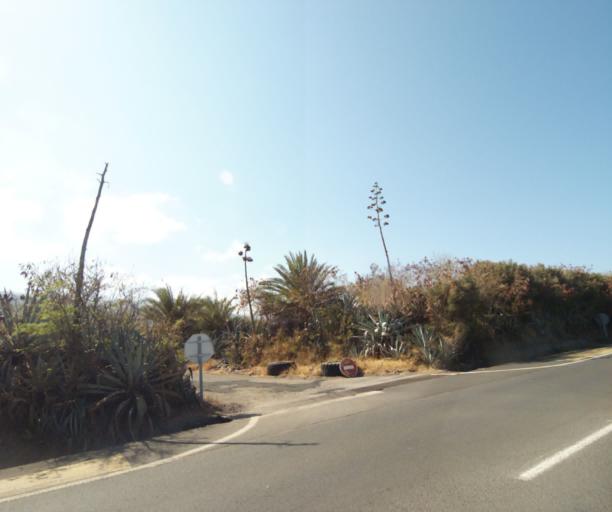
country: RE
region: Reunion
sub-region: Reunion
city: Trois-Bassins
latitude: -21.1115
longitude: 55.2560
